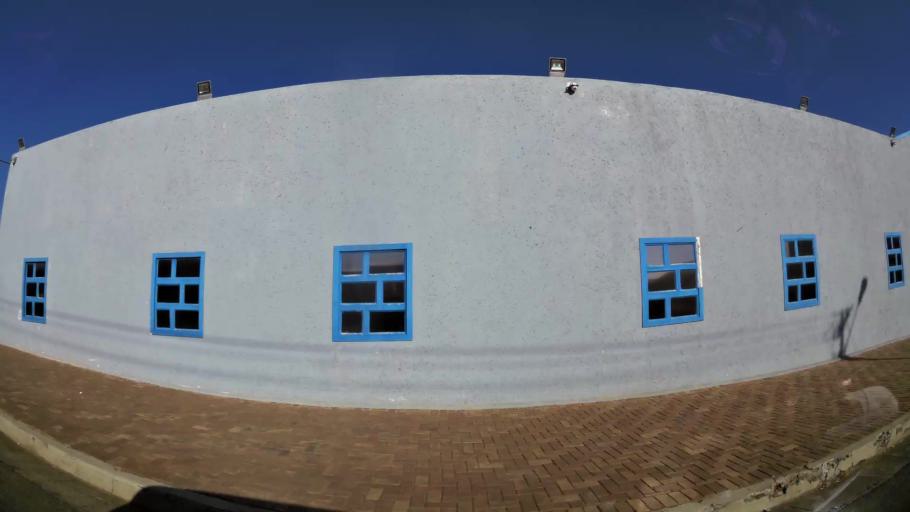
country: ZA
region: Gauteng
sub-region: City of Johannesburg Metropolitan Municipality
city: Roodepoort
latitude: -26.1619
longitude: 27.8624
